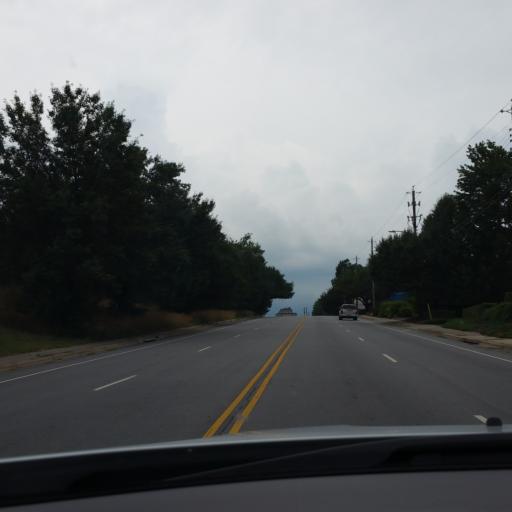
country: US
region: North Carolina
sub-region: Buncombe County
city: Asheville
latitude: 35.5857
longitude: -82.5562
